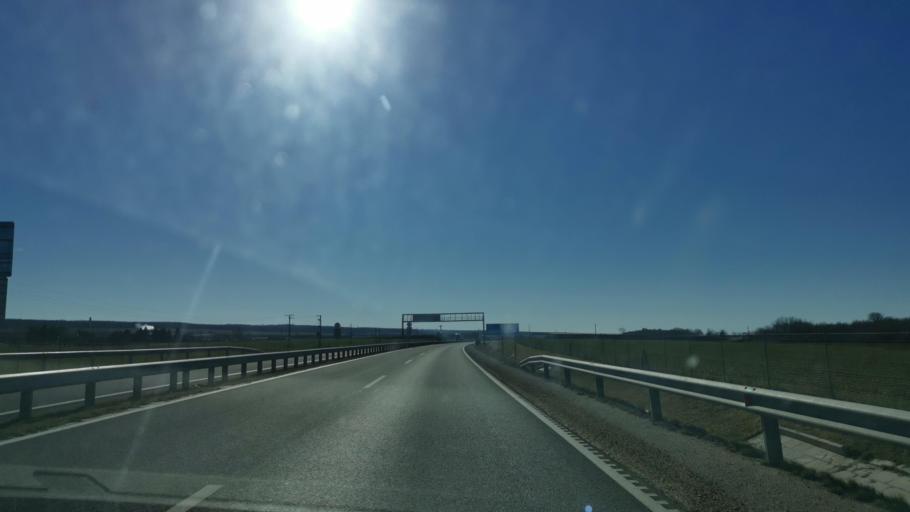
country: HU
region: Somogy
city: Balatonbereny
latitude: 46.6810
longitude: 17.2937
